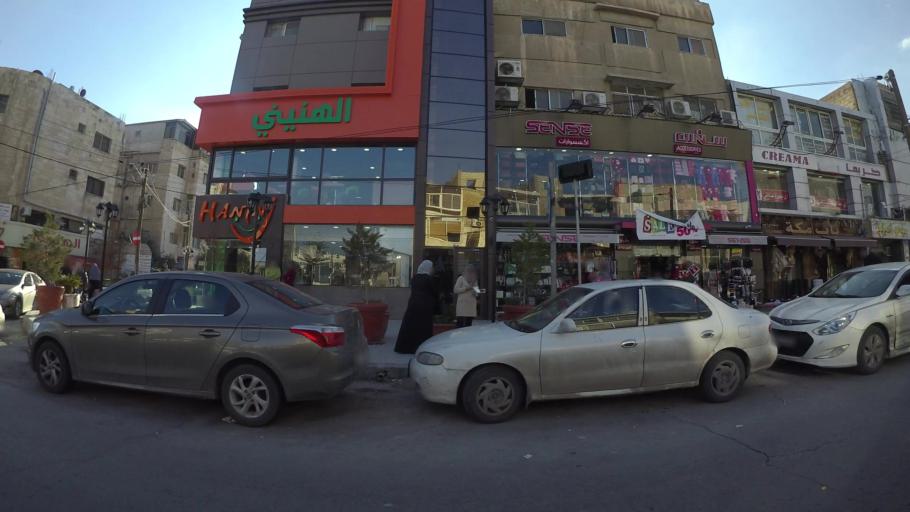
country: JO
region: Amman
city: Amman
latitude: 31.9736
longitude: 35.9503
